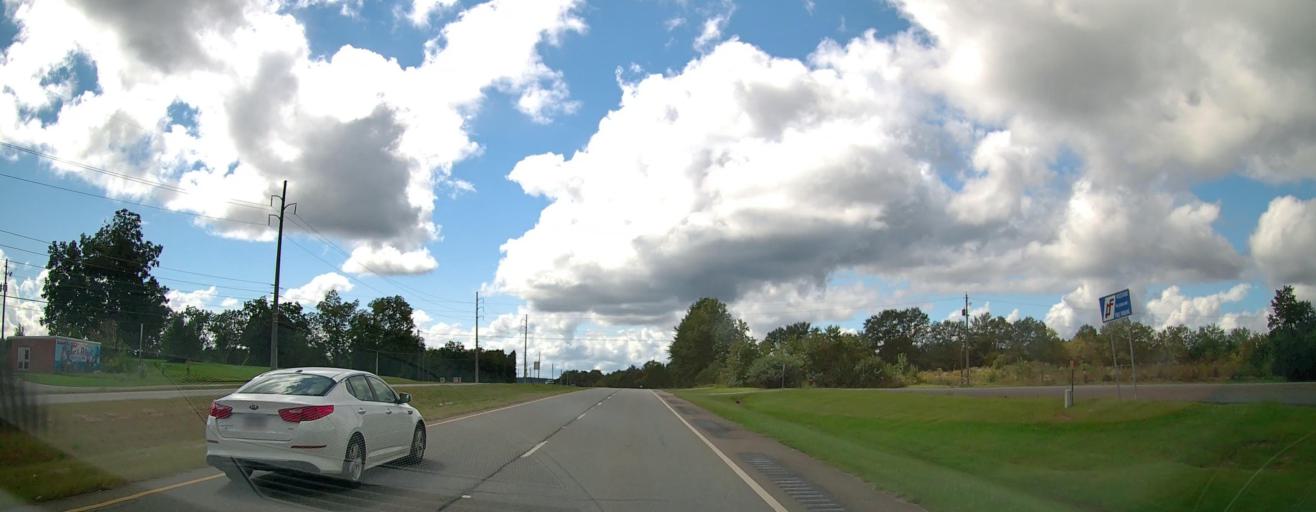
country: US
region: Georgia
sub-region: Baldwin County
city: Milledgeville
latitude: 33.0940
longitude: -83.2737
